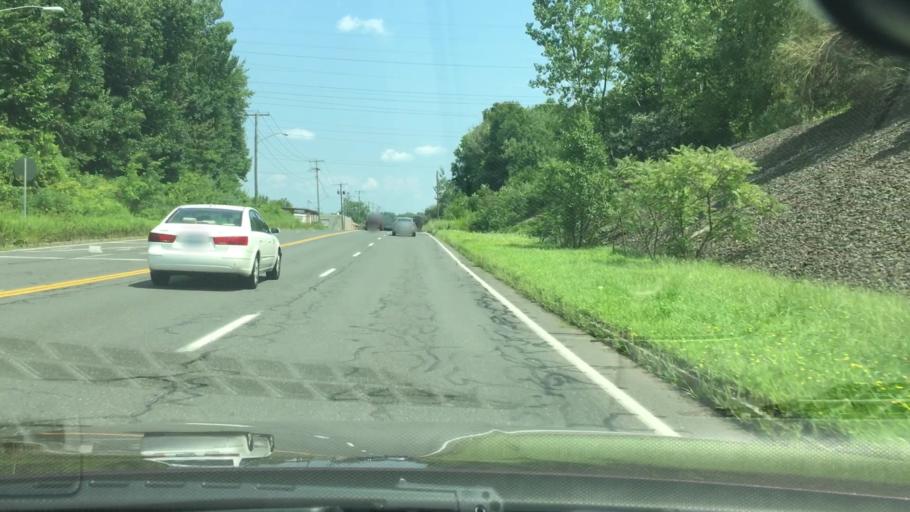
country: US
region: Connecticut
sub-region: Hartford County
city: East Hartford
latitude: 41.7939
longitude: -72.5684
